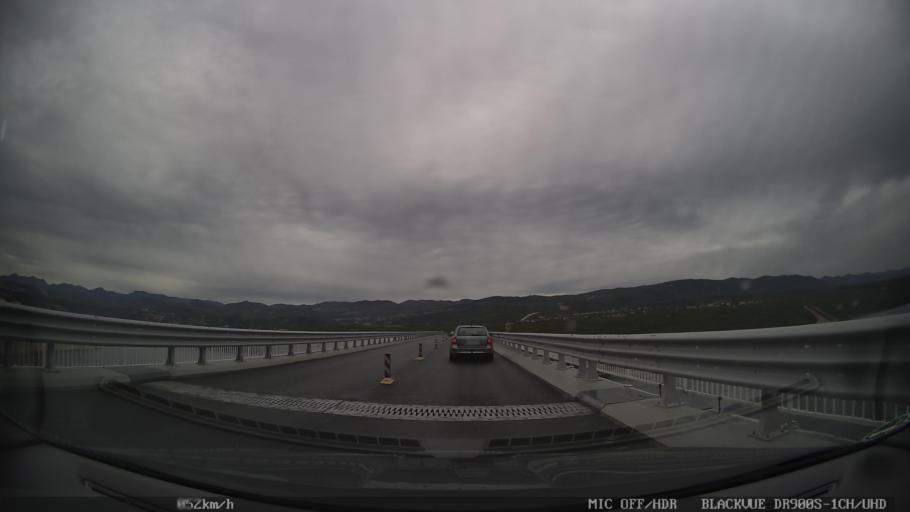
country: HR
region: Primorsko-Goranska
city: Kraljevica
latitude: 45.2465
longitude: 14.5680
